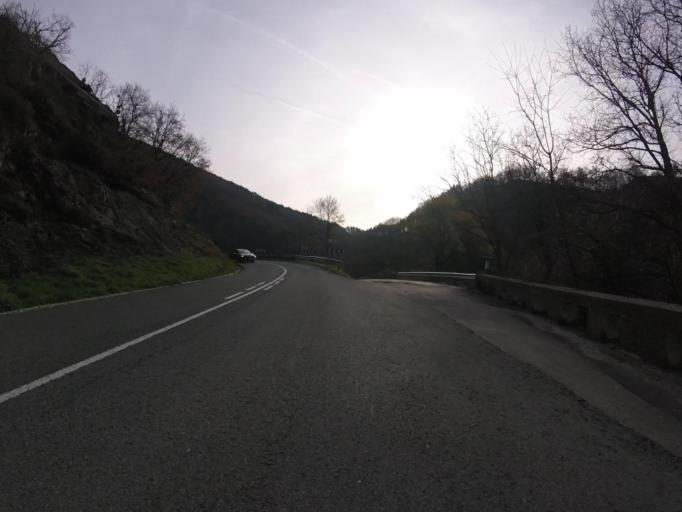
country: ES
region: Basque Country
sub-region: Provincia de Guipuzcoa
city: Elduayen
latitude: 43.1404
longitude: -1.9910
